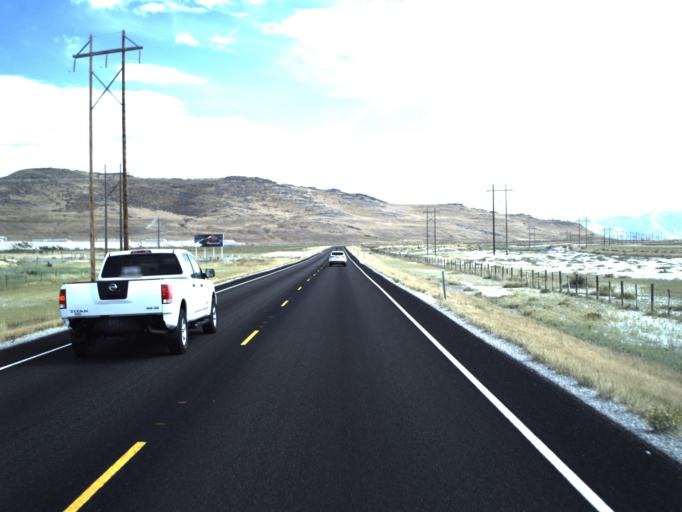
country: US
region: Utah
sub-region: Box Elder County
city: Tremonton
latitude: 41.6285
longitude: -112.4084
